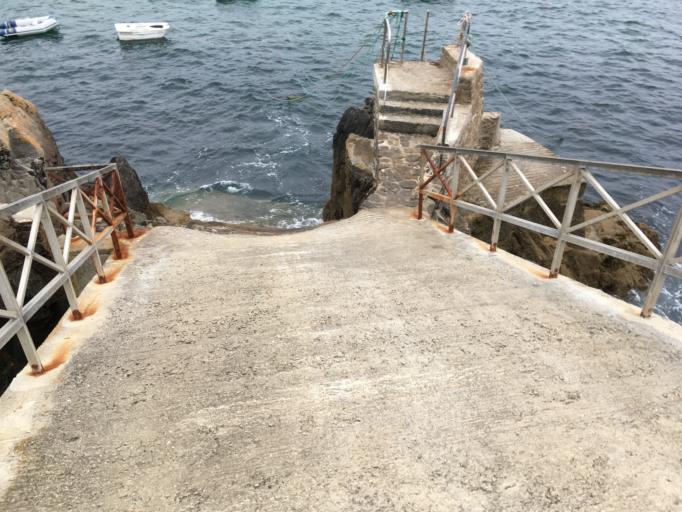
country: FR
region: Brittany
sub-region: Departement du Finistere
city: Plogoff
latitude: 48.0529
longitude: -4.7126
